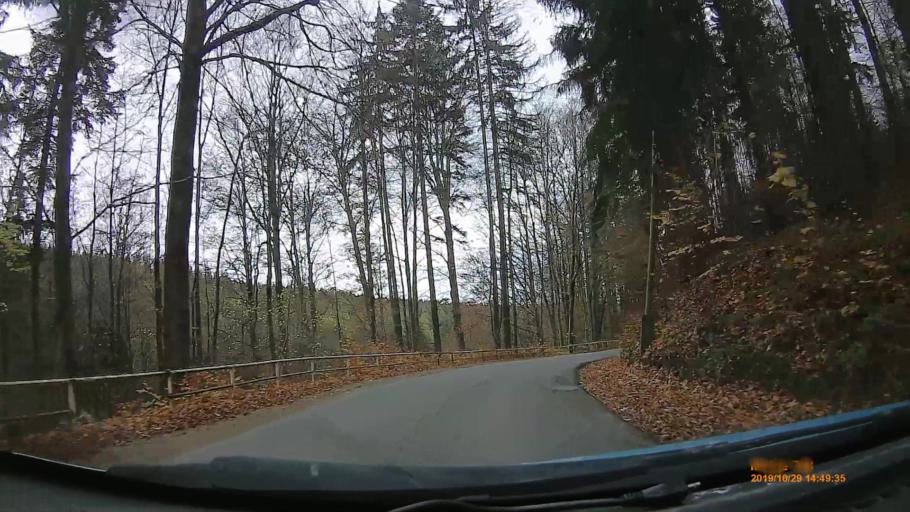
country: PL
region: Lower Silesian Voivodeship
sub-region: Powiat klodzki
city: Szczytna
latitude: 50.4330
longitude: 16.4364
